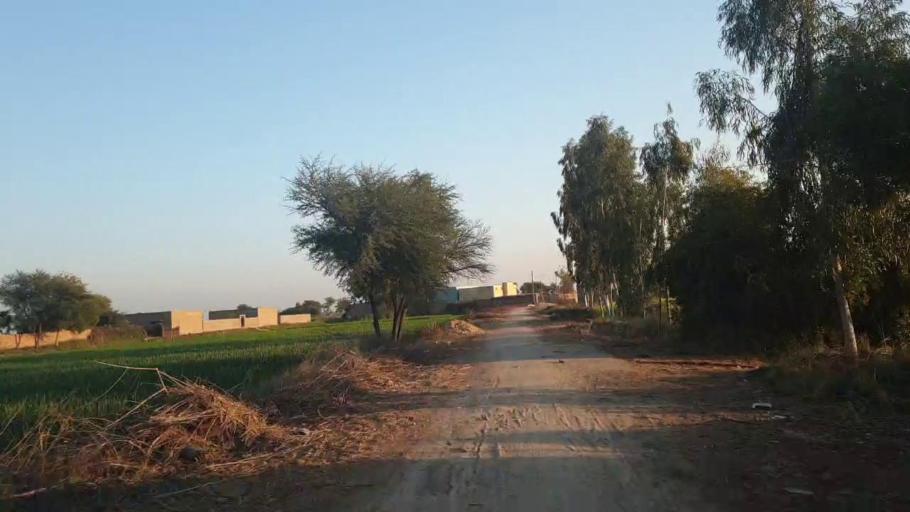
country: PK
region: Sindh
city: Khadro
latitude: 26.0751
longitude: 68.7006
